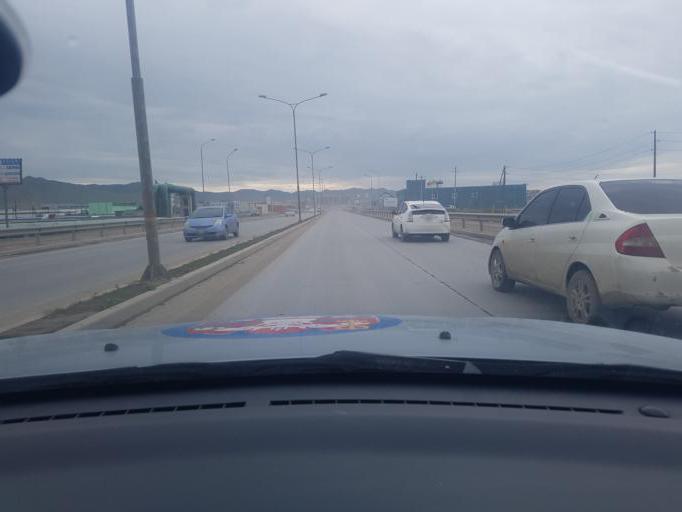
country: MN
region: Ulaanbaatar
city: Ulaanbaatar
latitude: 47.8895
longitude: 106.7853
